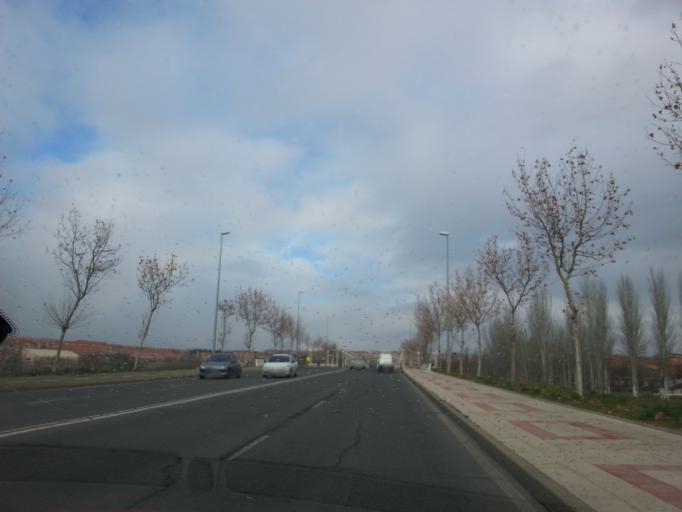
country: ES
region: Castille and Leon
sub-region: Provincia de Salamanca
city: Salamanca
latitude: 40.9600
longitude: -5.6813
